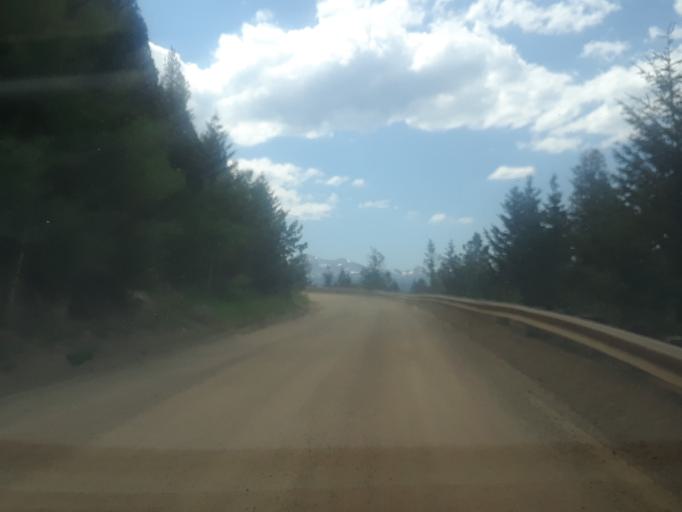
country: US
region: Colorado
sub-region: Boulder County
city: Boulder
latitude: 40.0707
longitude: -105.3897
